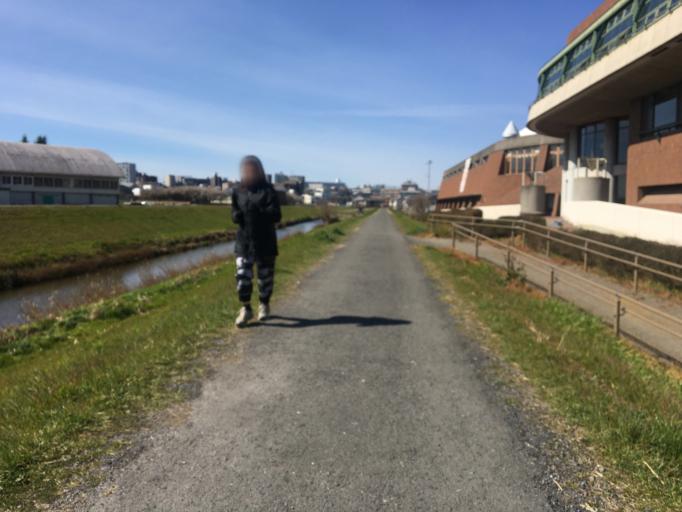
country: JP
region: Saitama
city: Asaka
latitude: 35.8162
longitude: 139.5993
